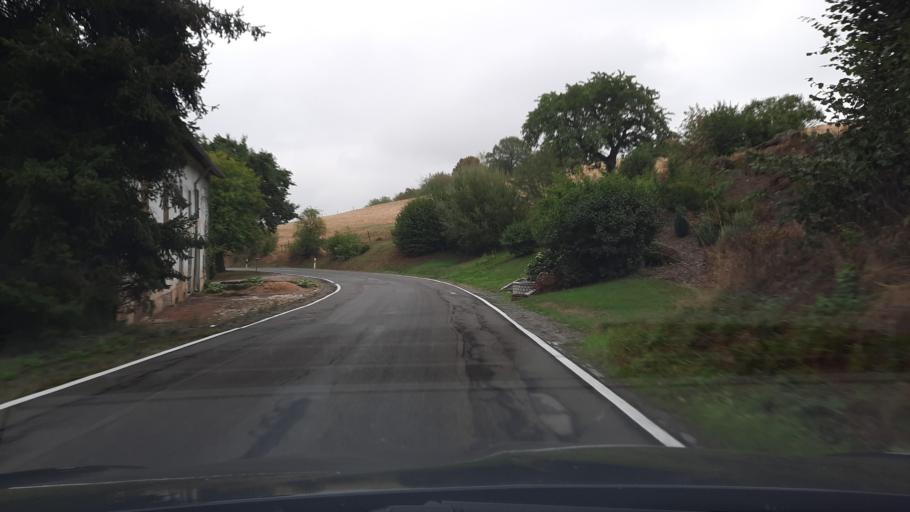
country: DE
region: Rheinland-Pfalz
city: Franzenheim
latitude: 49.6872
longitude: 6.6739
